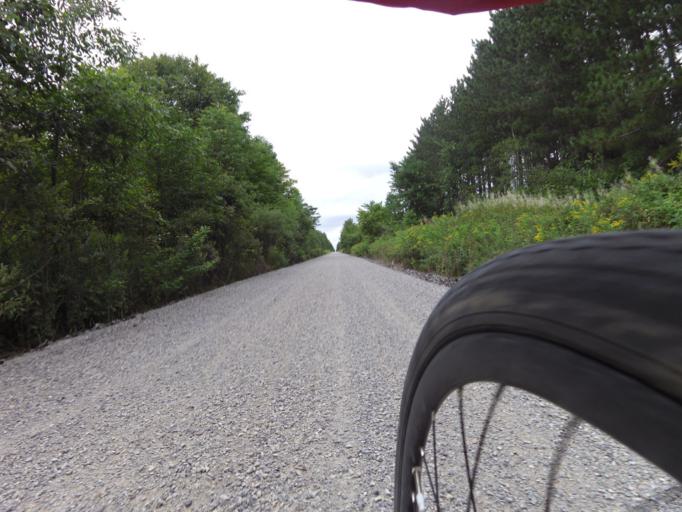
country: CA
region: Ontario
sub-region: Lanark County
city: Smiths Falls
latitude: 44.9660
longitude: -76.0529
